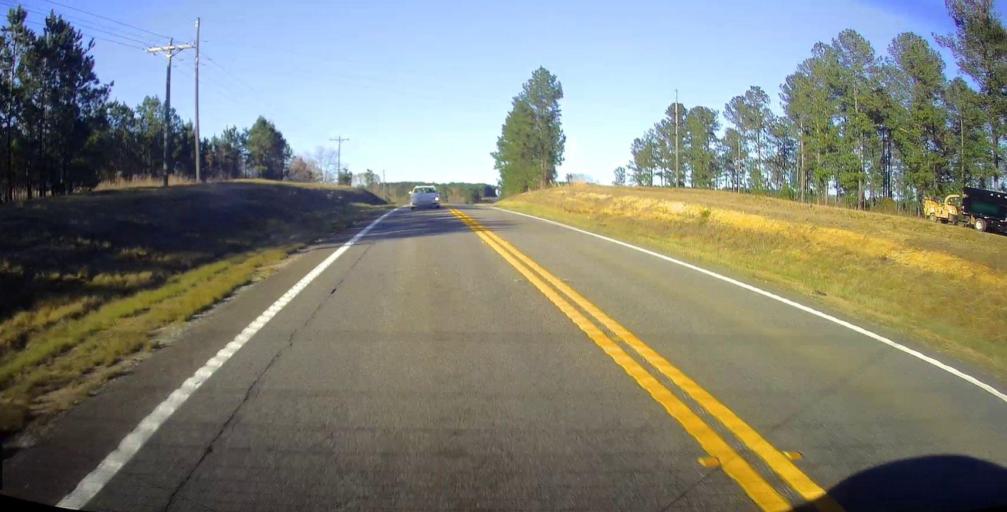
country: US
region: Georgia
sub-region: Taylor County
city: Butler
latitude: 32.4740
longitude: -84.3575
